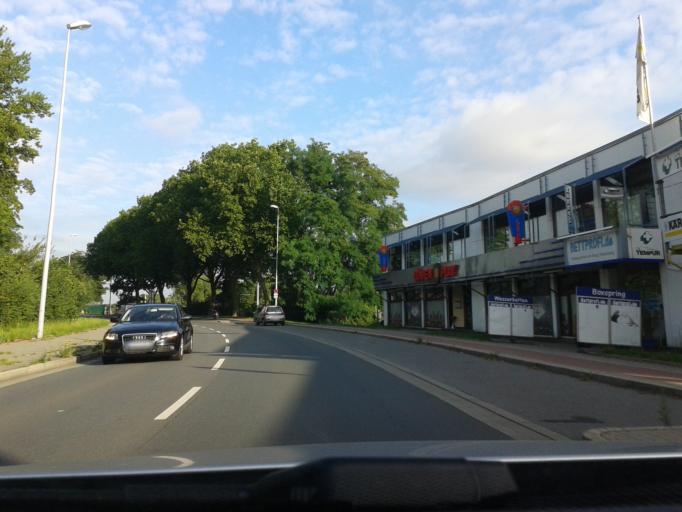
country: DE
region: North Rhine-Westphalia
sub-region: Regierungsbezirk Dusseldorf
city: Muelheim (Ruhr)
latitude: 51.4404
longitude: 6.8313
